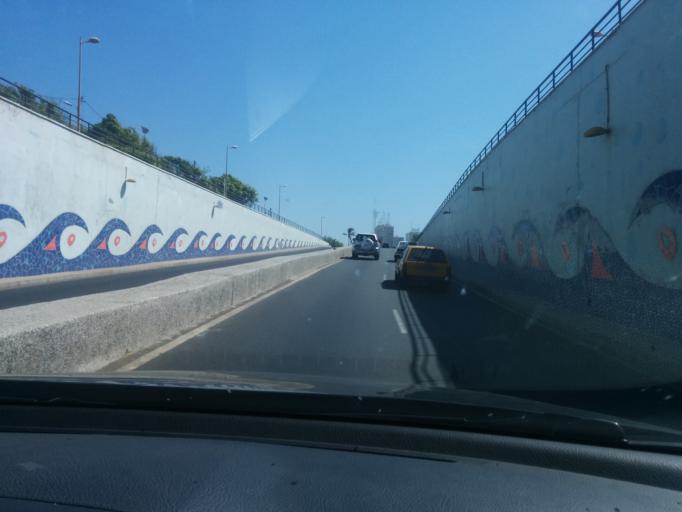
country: SN
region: Dakar
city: Dakar
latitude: 14.6734
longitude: -17.4500
